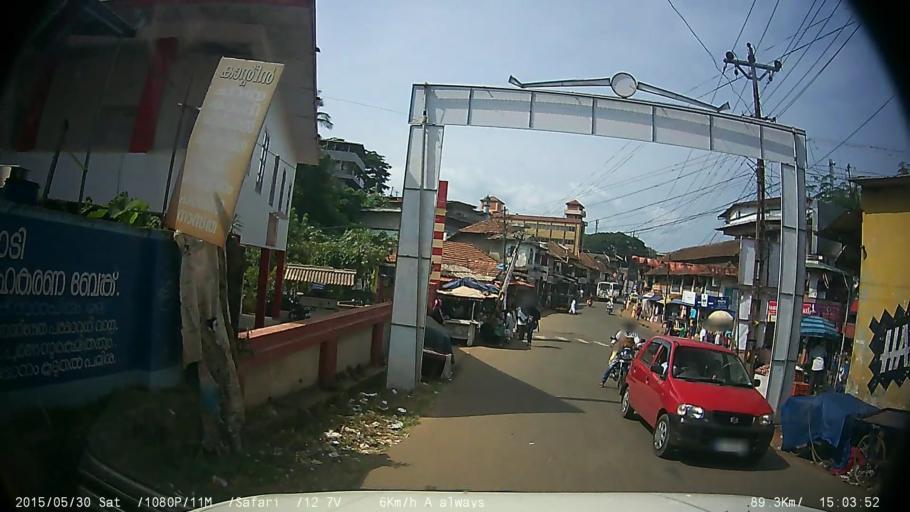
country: IN
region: Kerala
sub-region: Wayanad
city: Panamaram
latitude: 11.8019
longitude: 76.0027
